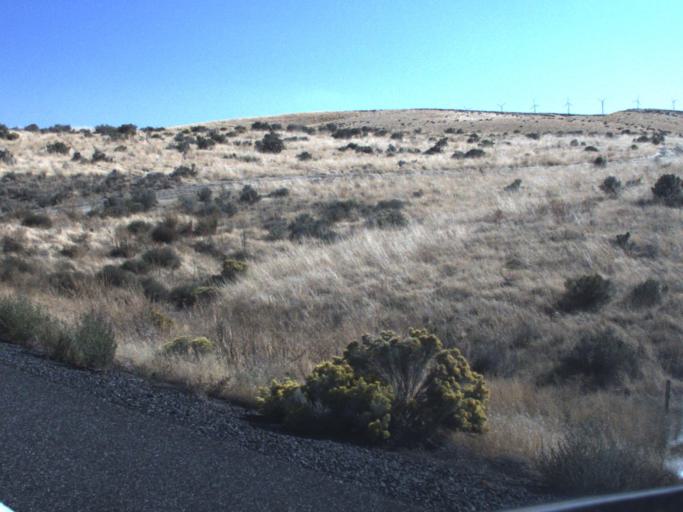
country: US
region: Washington
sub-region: Benton County
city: Highland
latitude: 46.1429
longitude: -119.1102
